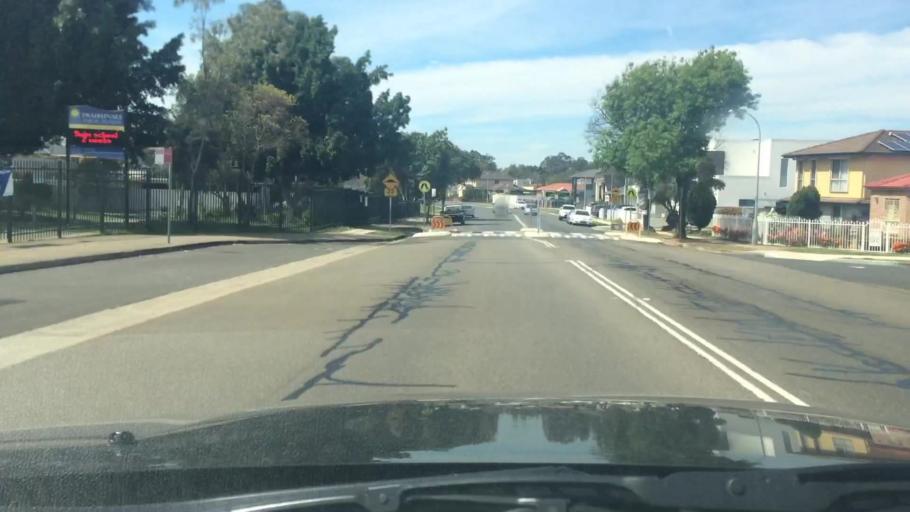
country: AU
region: New South Wales
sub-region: Fairfield
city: Cabramatta West
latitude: -33.8672
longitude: 150.8911
